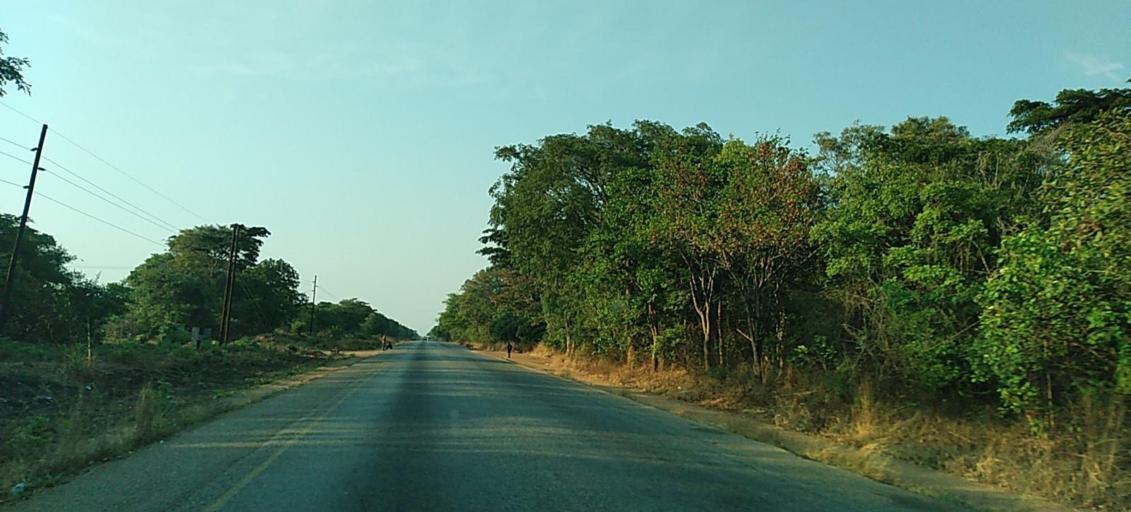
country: ZM
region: Copperbelt
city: Ndola
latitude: -13.2222
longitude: 28.6807
